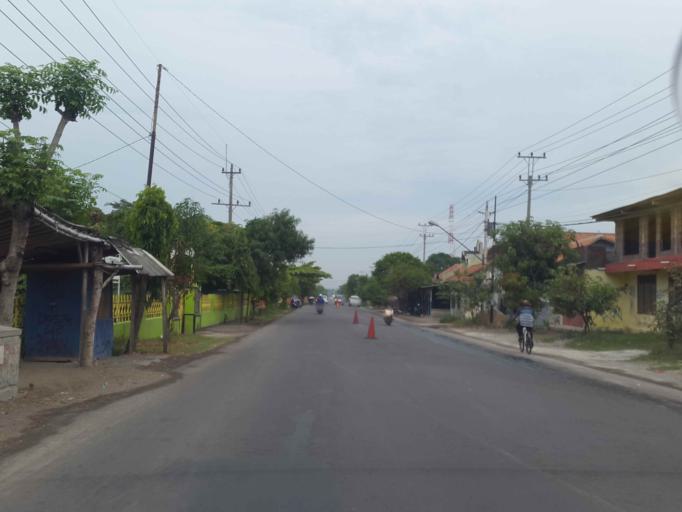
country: ID
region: Central Java
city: Adiwerna
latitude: -6.9241
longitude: 109.1259
